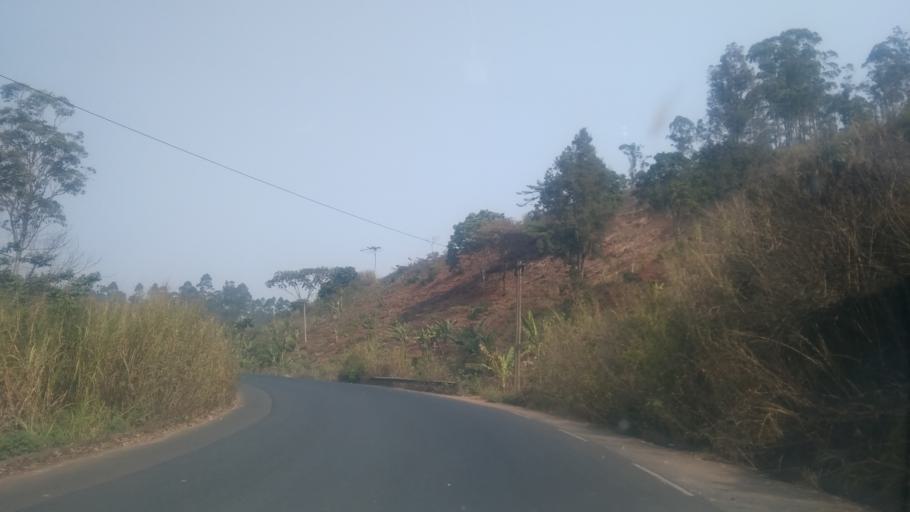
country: CM
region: West
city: Dschang
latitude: 5.4065
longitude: 10.0152
